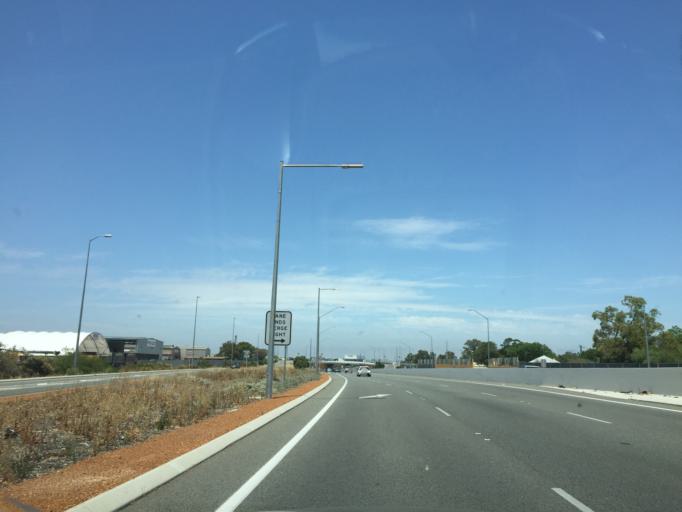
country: AU
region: Western Australia
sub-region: Belmont
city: Kewdale
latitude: -31.9697
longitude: 115.9523
